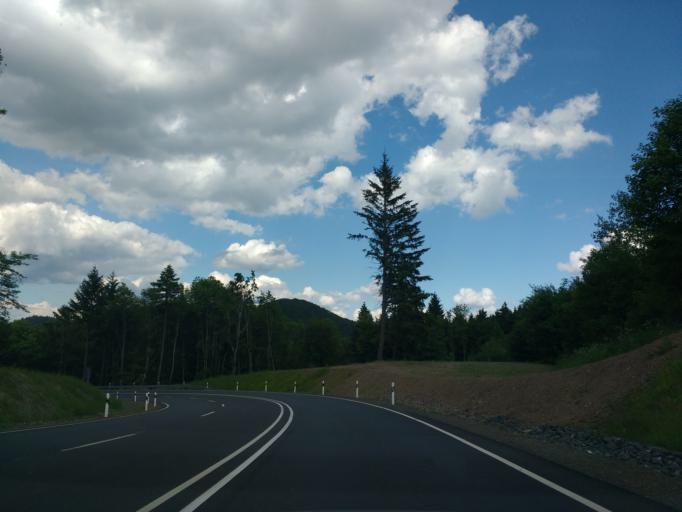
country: DE
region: Hesse
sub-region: Regierungsbezirk Giessen
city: Biedenkopf
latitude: 50.9423
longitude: 8.5562
